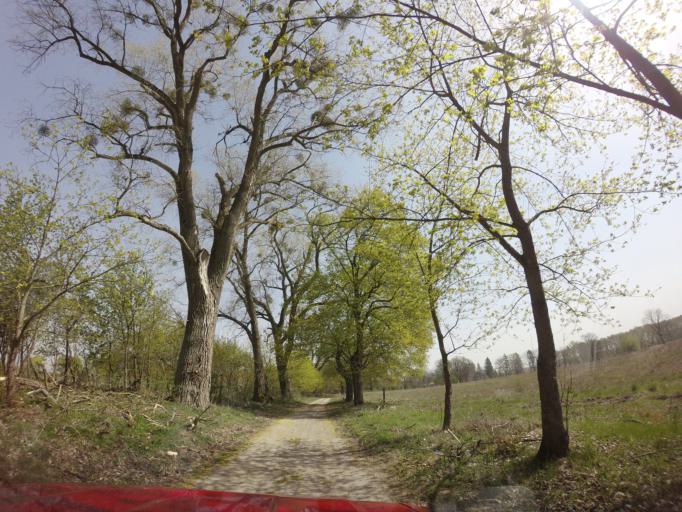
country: PL
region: West Pomeranian Voivodeship
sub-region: Powiat choszczenski
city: Recz
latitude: 53.2439
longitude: 15.6367
